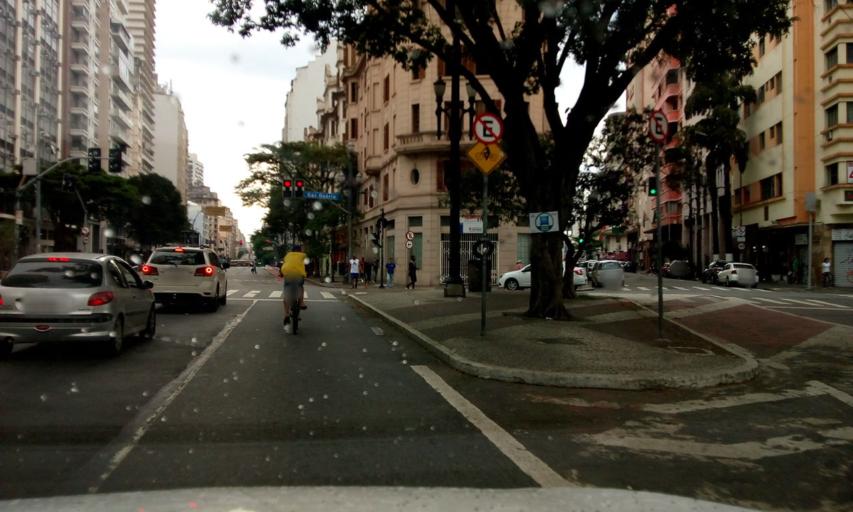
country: BR
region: Sao Paulo
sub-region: Sao Paulo
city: Sao Paulo
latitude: -23.5399
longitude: -46.6445
